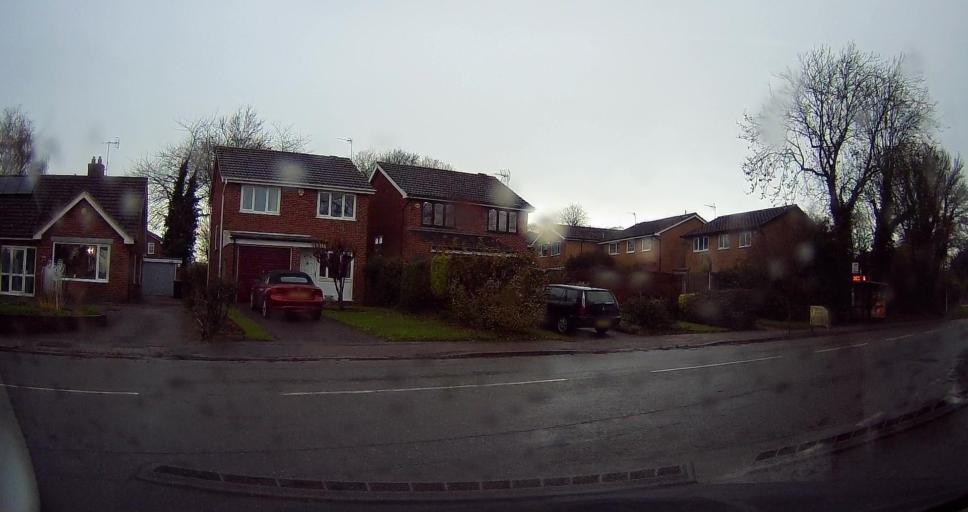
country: GB
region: England
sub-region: Nottinghamshire
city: Kimberley
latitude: 53.0065
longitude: -1.2529
